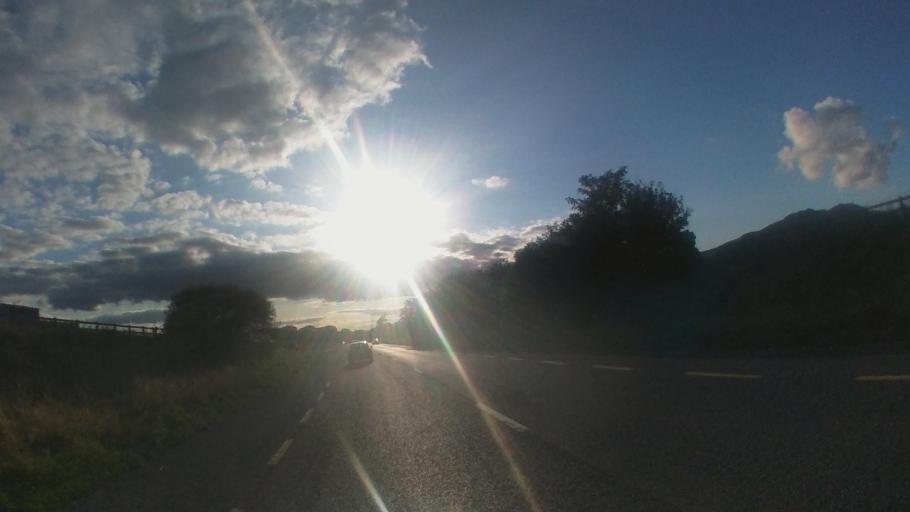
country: IE
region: Leinster
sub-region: Lu
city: Carlingford
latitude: 53.9977
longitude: -6.2347
